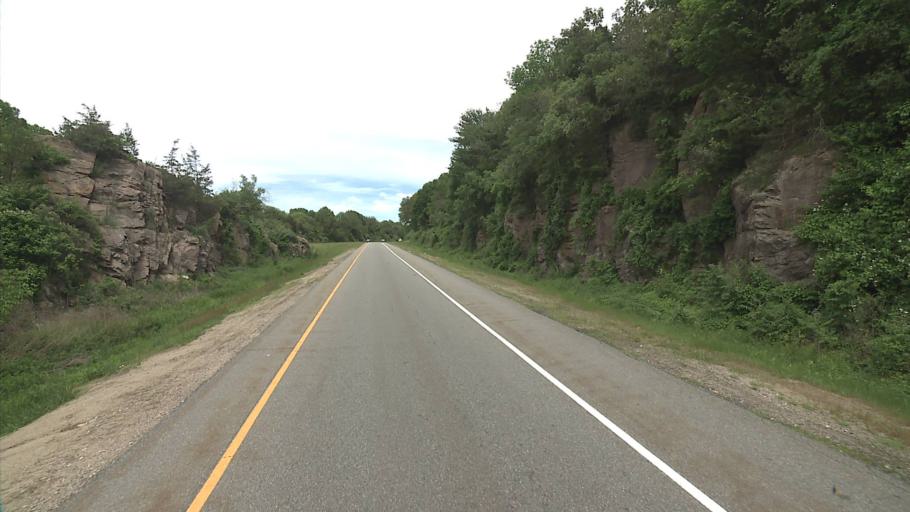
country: US
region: Connecticut
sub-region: New London County
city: Pawcatuck
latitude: 41.4203
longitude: -71.8424
